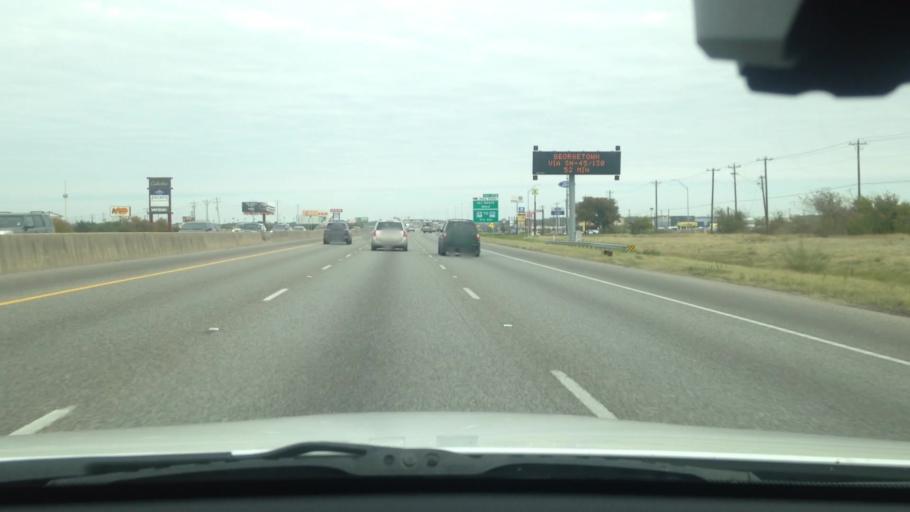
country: US
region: Texas
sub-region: Hays County
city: Buda
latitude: 30.0817
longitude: -97.8227
